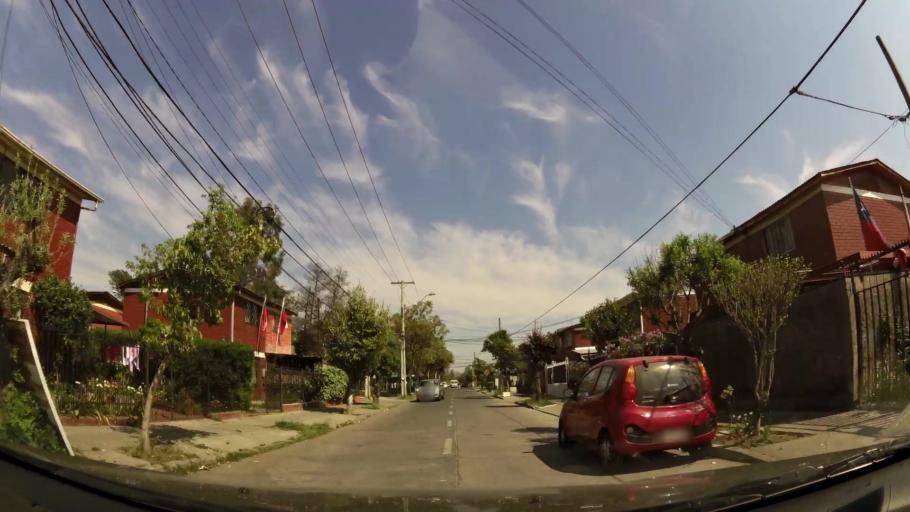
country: CL
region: Santiago Metropolitan
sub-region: Provincia de Santiago
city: La Pintana
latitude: -33.5795
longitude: -70.6024
